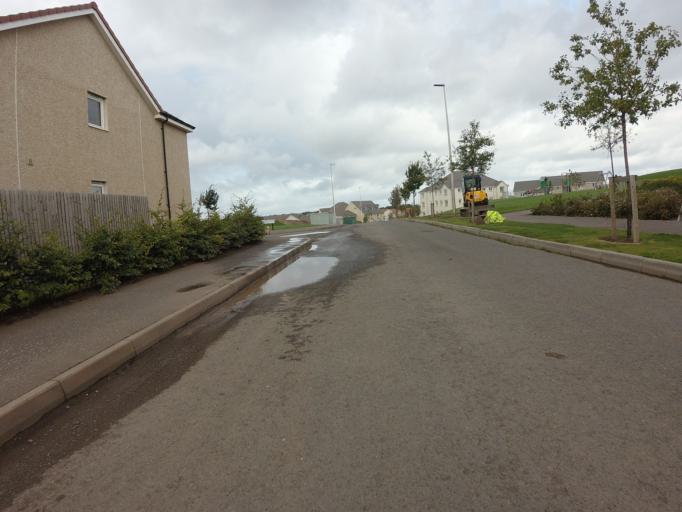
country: GB
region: Scotland
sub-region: East Lothian
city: Musselburgh
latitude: 55.9408
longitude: -3.0279
